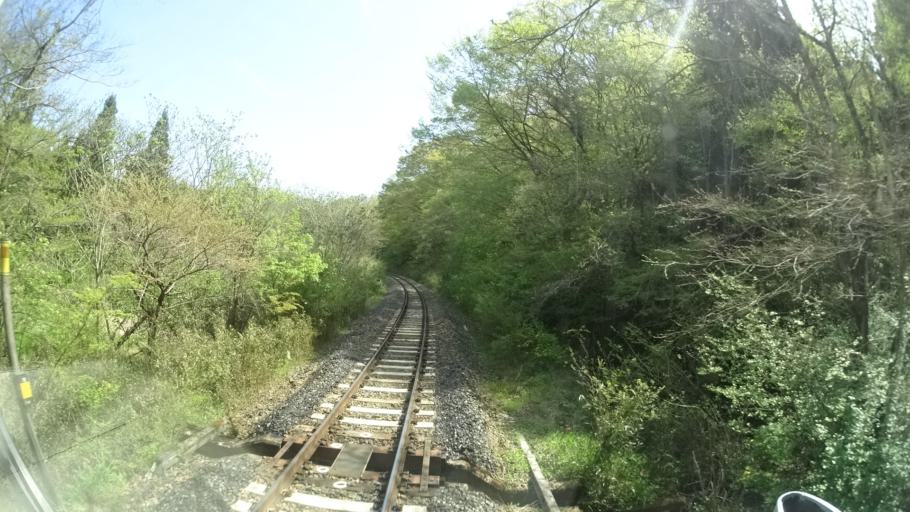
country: JP
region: Iwate
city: Ofunato
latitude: 38.9104
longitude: 141.5311
